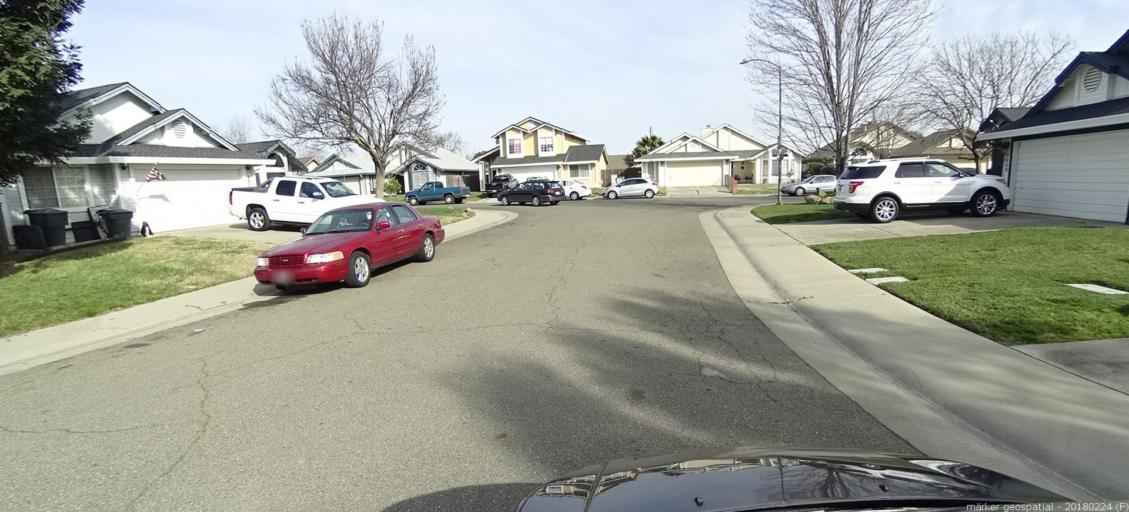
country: US
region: California
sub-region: Sacramento County
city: Rio Linda
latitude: 38.6933
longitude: -121.4606
